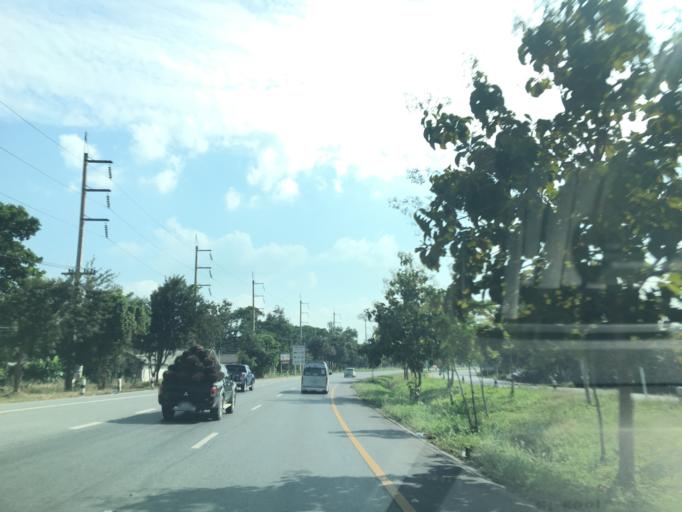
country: TH
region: Chiang Rai
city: Mae Lao
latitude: 19.7105
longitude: 99.7202
